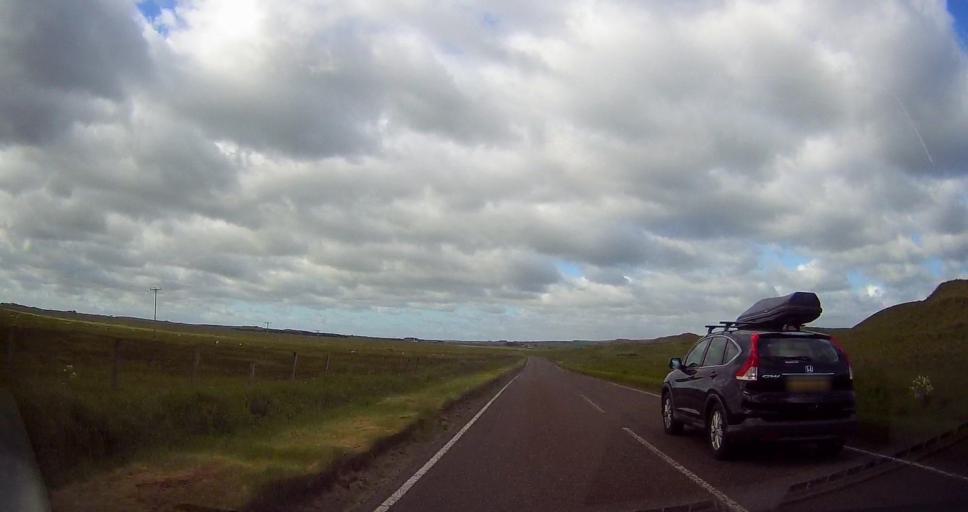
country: GB
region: Scotland
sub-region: Highland
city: Thurso
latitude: 58.6068
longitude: -3.3453
